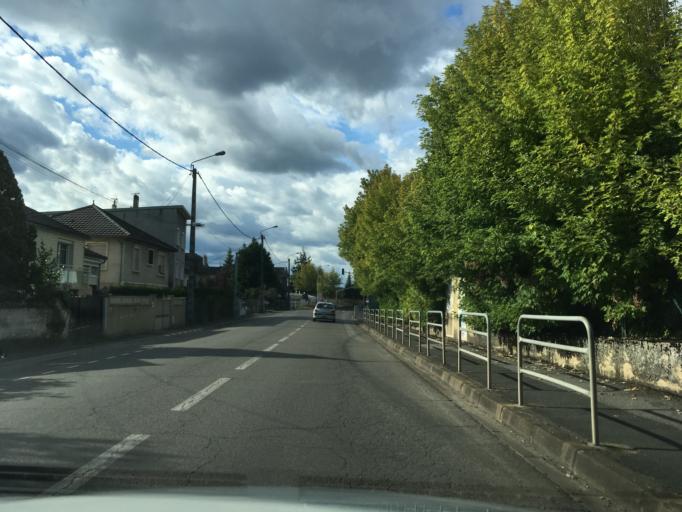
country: FR
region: Limousin
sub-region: Departement de la Correze
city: Malemort-sur-Correze
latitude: 45.1546
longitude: 1.5577
